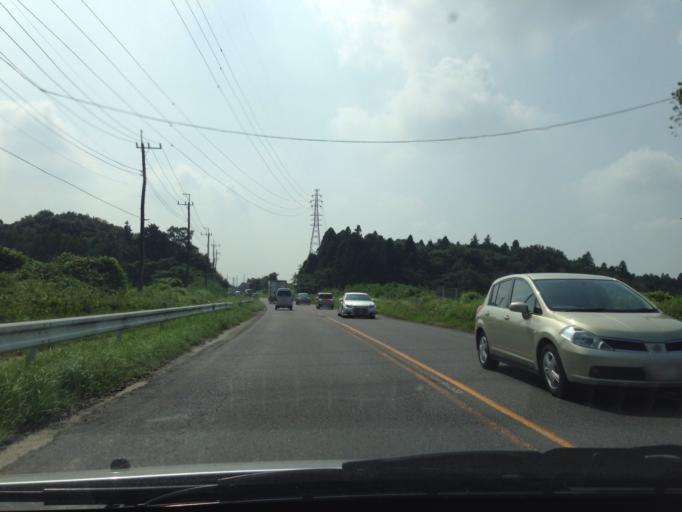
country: JP
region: Ibaraki
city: Ami
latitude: 36.0242
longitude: 140.2375
